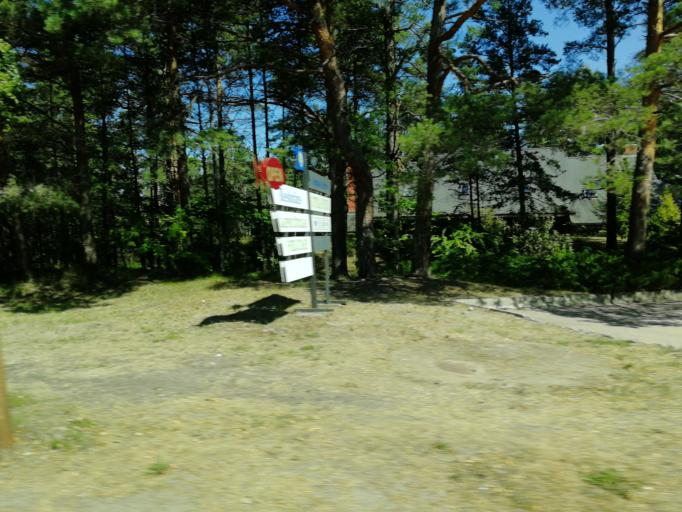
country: LV
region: Rojas
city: Roja
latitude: 57.5078
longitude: 22.7983
